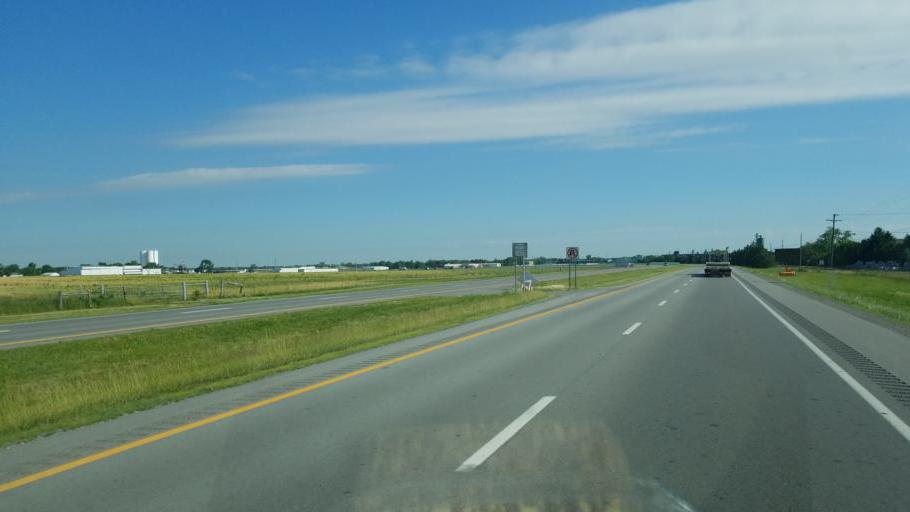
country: US
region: Ohio
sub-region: Hancock County
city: Findlay
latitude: 41.0132
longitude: -83.6602
